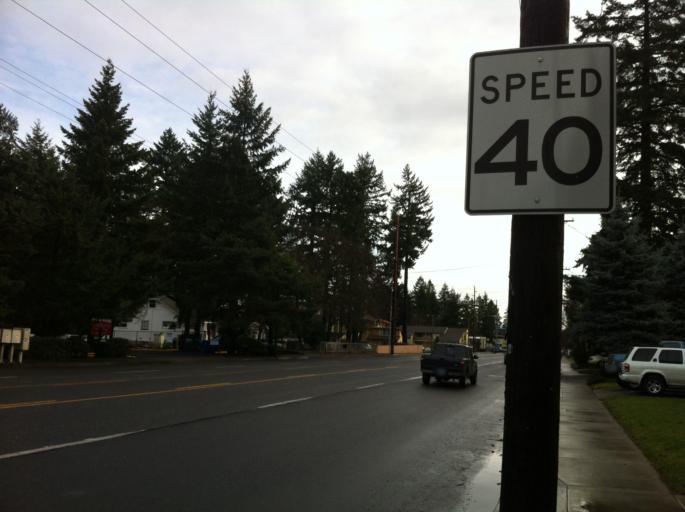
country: US
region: Oregon
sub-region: Multnomah County
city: Lents
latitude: 45.5190
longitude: -122.5234
